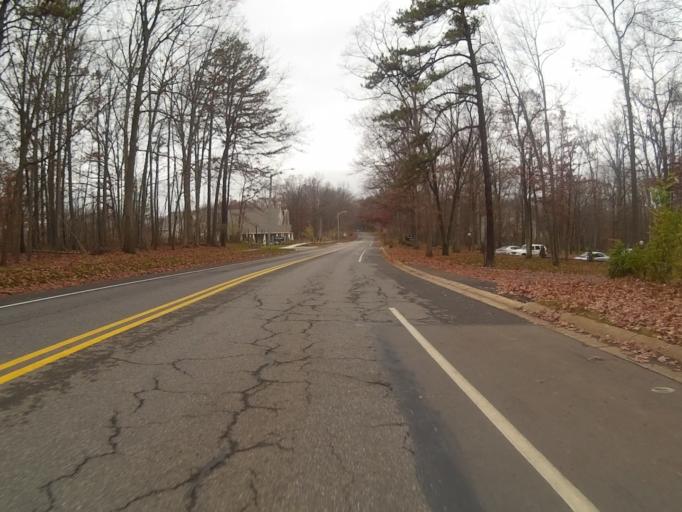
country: US
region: Pennsylvania
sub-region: Centre County
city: Park Forest Village
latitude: 40.8237
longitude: -77.8900
